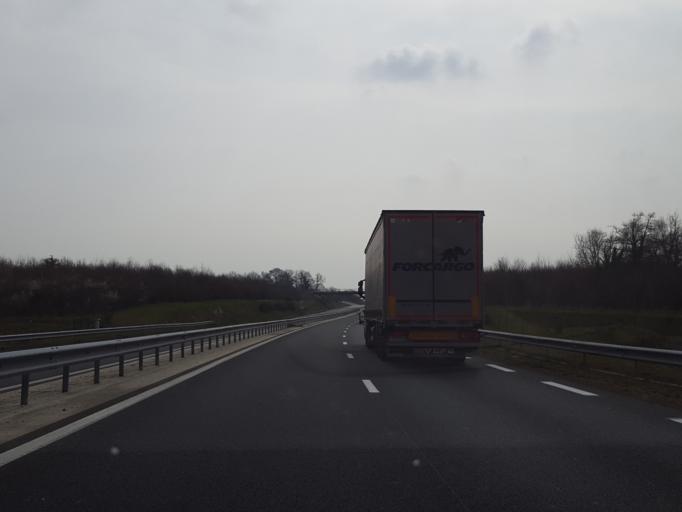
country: FR
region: Pays de la Loire
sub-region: Departement de la Vendee
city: Dompierre-sur-Yon
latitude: 46.6765
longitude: -1.3665
